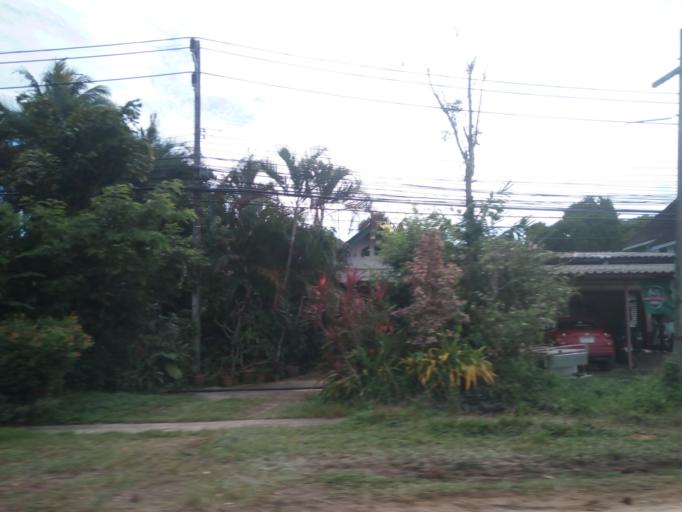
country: TH
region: Phuket
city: Mueang Phuket
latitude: 7.8345
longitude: 98.3963
